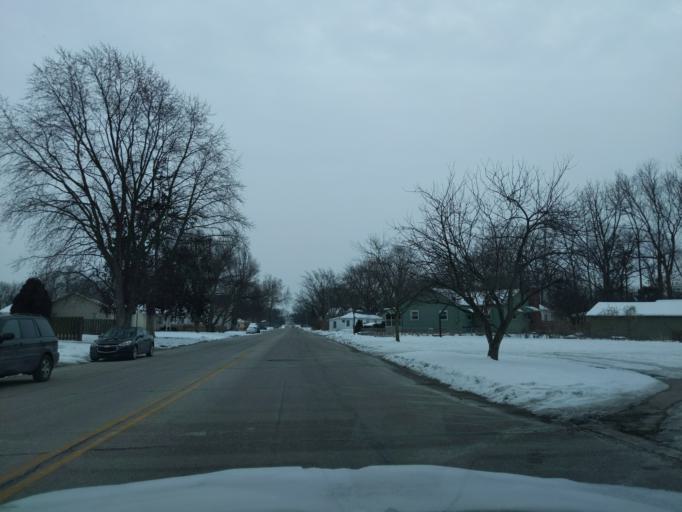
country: US
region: Indiana
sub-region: Tippecanoe County
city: Lafayette
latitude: 40.4060
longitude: -86.8762
